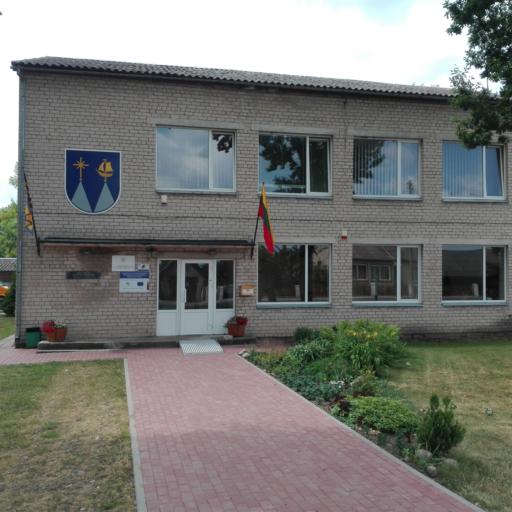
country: LT
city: Obeliai
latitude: 56.1172
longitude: 25.0061
